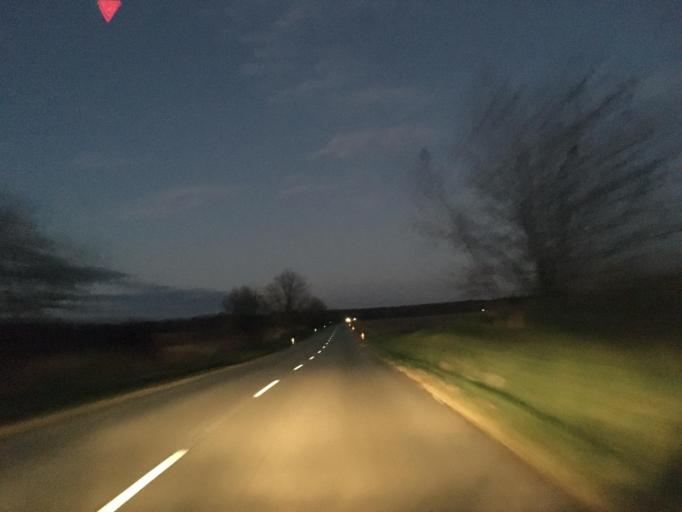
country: SK
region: Nitriansky
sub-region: Okres Komarno
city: Hurbanovo
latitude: 47.9180
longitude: 18.2262
